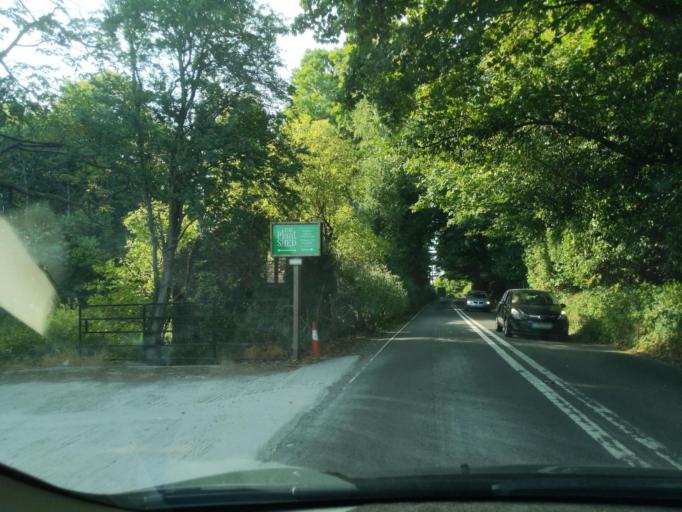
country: GB
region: England
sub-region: Devon
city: Winkleigh
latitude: 50.8888
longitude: -3.8756
